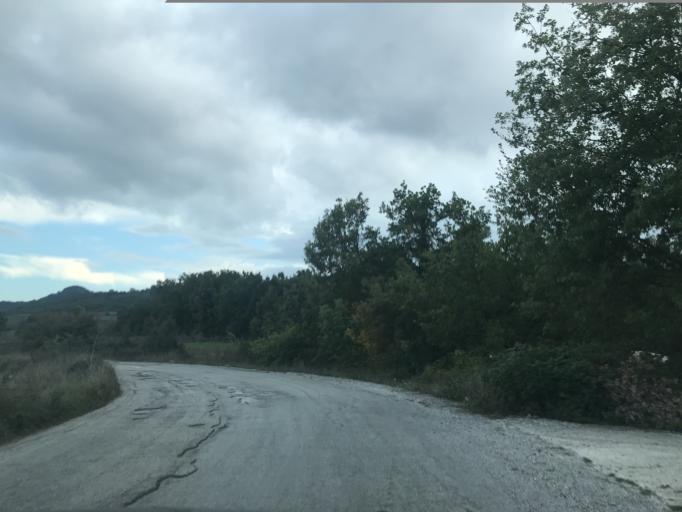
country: IT
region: Molise
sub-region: Provincia di Campobasso
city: Duronia
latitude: 41.6755
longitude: 14.4529
